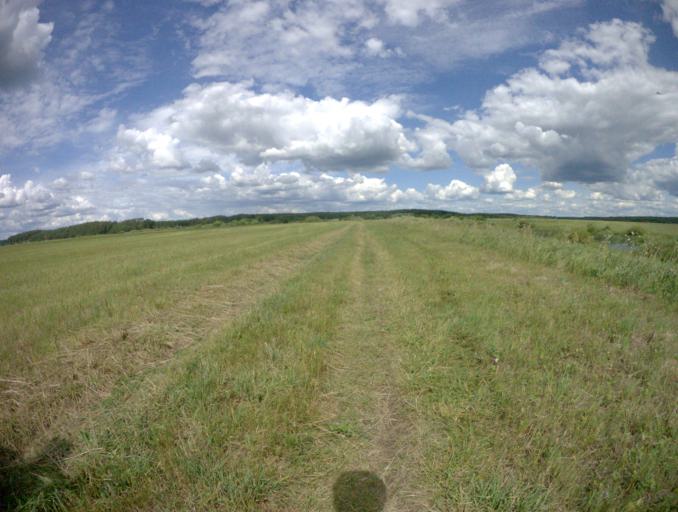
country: RU
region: Vladimir
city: Orgtrud
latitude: 56.3107
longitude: 40.6897
